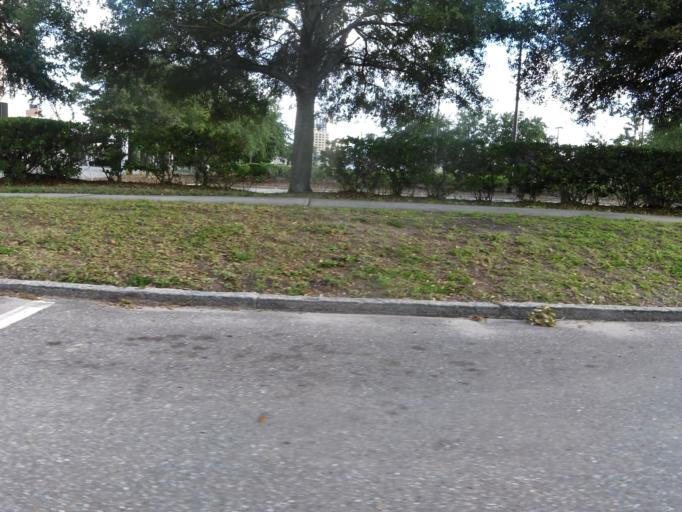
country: US
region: Florida
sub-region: Duval County
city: Jacksonville
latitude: 30.3369
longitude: -81.6594
